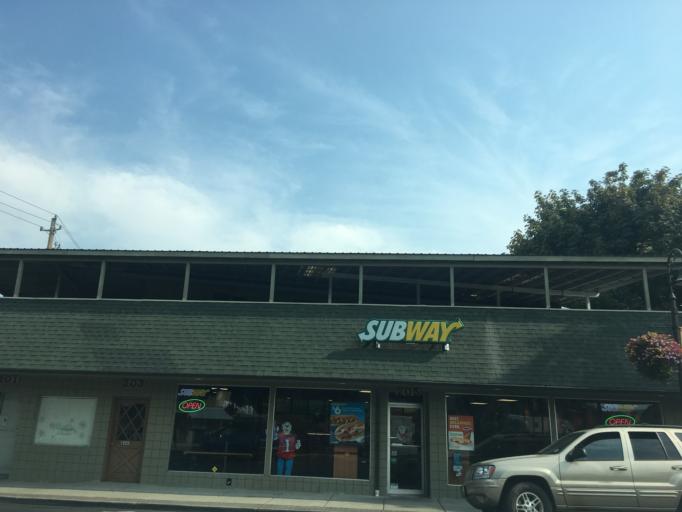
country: US
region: Oregon
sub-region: Jackson County
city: Rogue River
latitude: 42.4335
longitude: -123.1687
